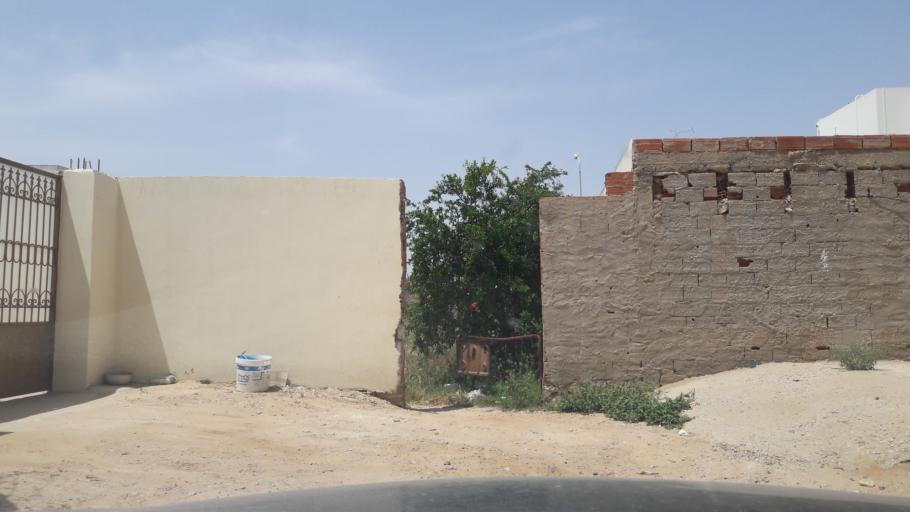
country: TN
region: Safaqis
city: Sfax
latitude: 34.7778
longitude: 10.7540
